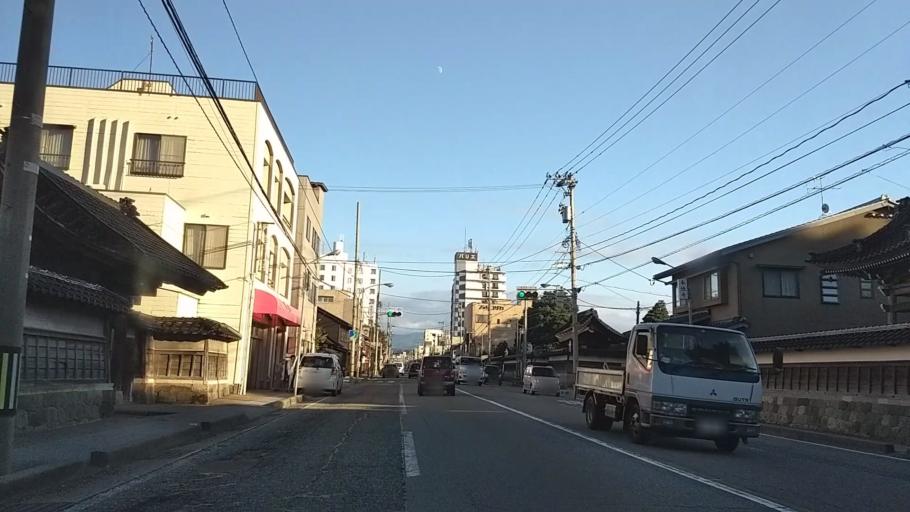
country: JP
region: Ishikawa
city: Nonoichi
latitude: 36.5526
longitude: 136.6536
